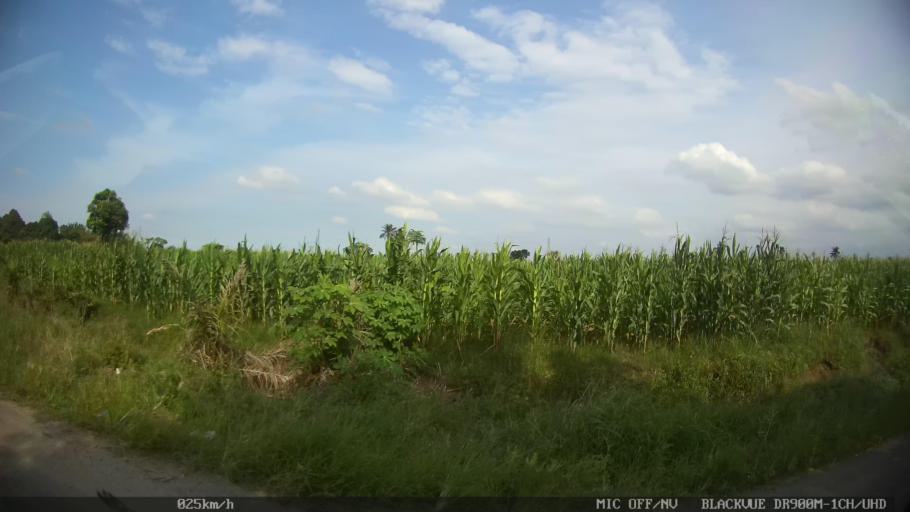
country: ID
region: North Sumatra
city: Percut
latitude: 3.5724
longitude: 98.7778
